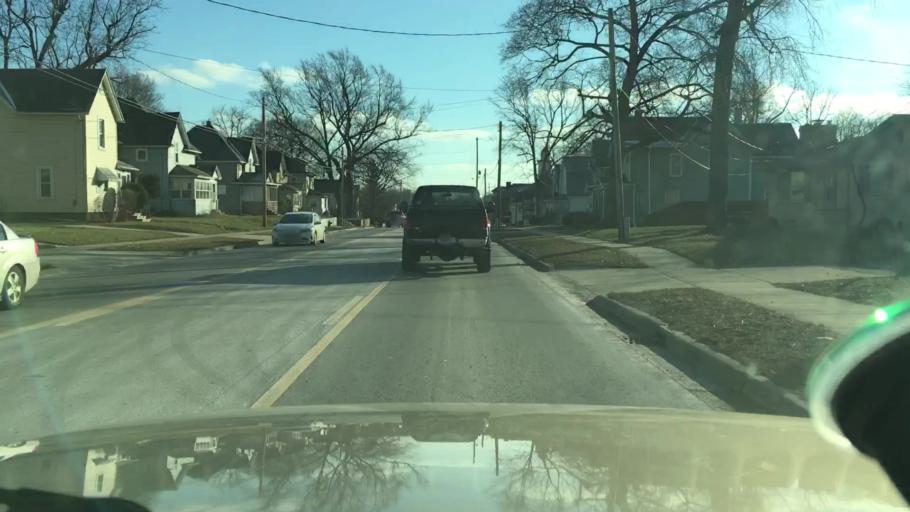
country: US
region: Michigan
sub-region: Jackson County
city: Jackson
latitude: 42.2580
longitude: -84.4234
